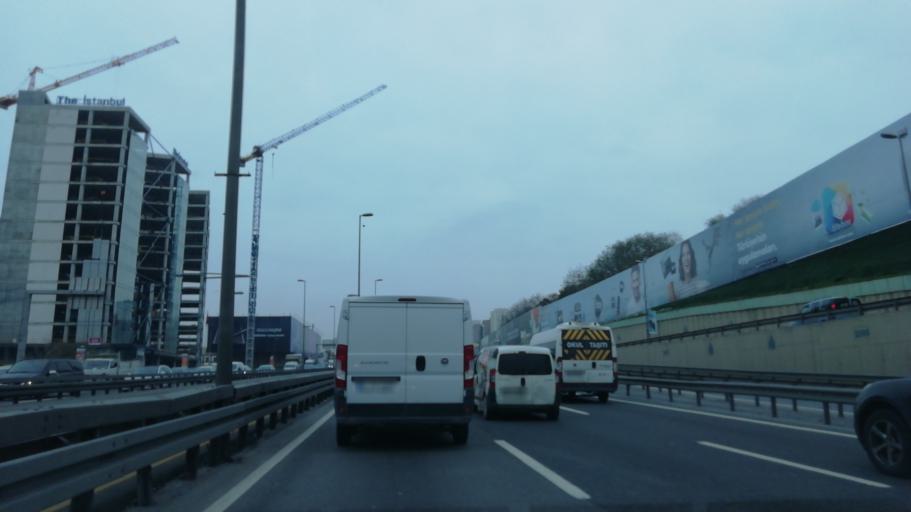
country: TR
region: Istanbul
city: guengoeren merter
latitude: 41.0092
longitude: 28.8999
